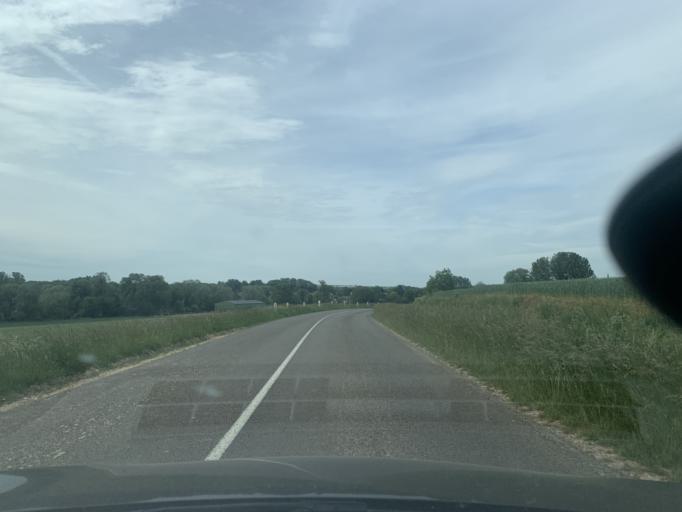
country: FR
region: Nord-Pas-de-Calais
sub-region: Departement du Nord
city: Marcoing
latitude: 50.1291
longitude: 3.1818
